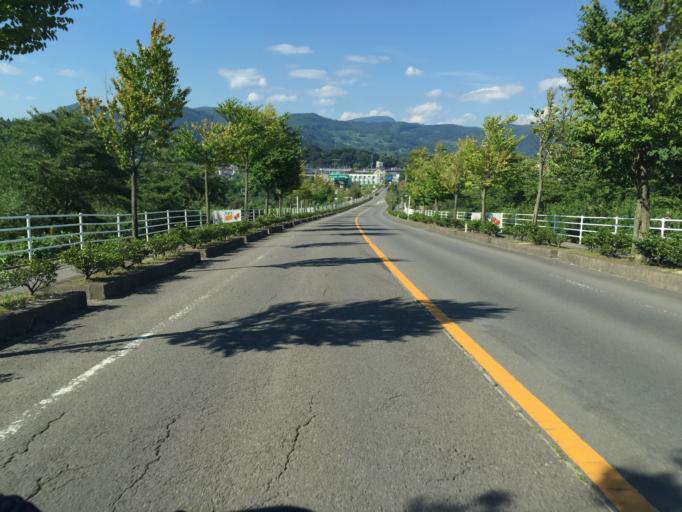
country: JP
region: Fukushima
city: Fukushima-shi
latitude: 37.8218
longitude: 140.4431
